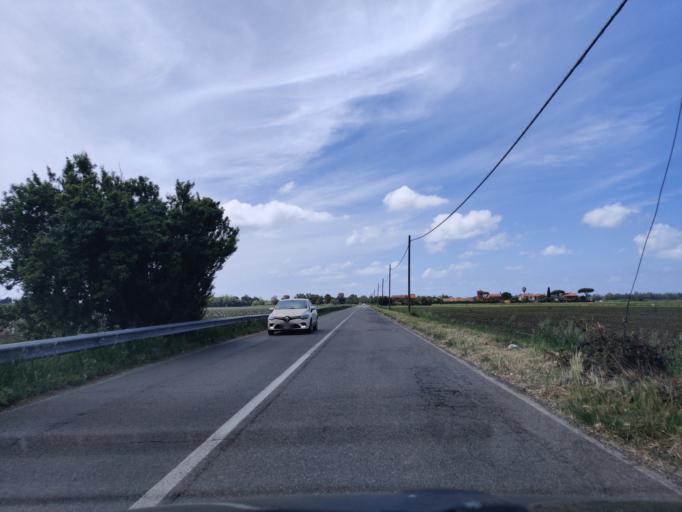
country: IT
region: Latium
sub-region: Citta metropolitana di Roma Capitale
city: Maccarese
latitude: 41.8841
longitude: 12.2209
